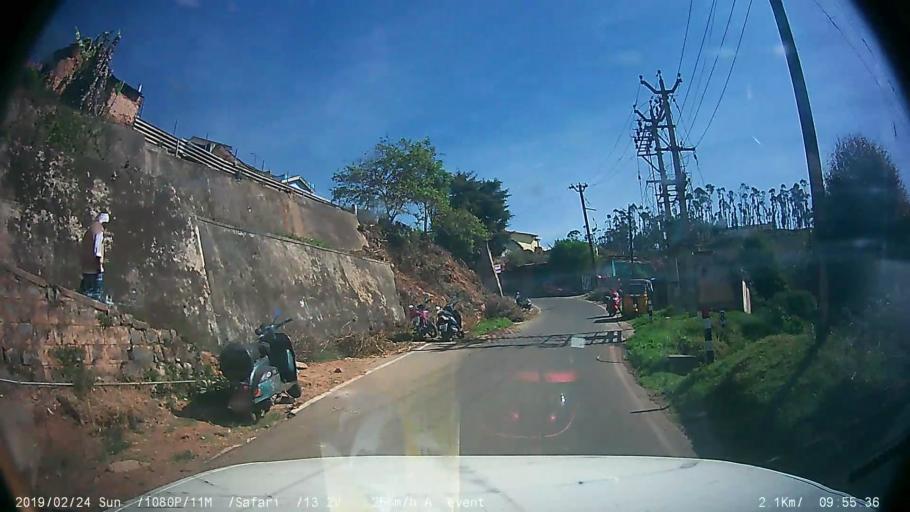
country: IN
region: Tamil Nadu
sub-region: Nilgiri
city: Wellington
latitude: 11.3572
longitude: 76.7718
